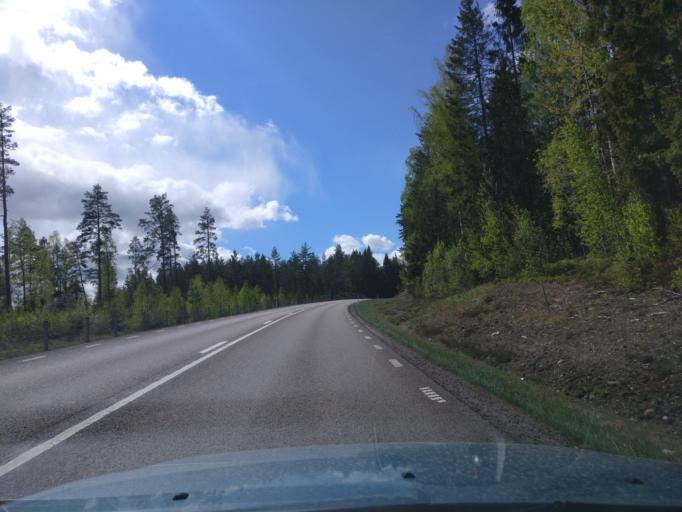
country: SE
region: Vaermland
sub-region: Karlstads Kommun
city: Molkom
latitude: 59.5859
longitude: 13.6844
